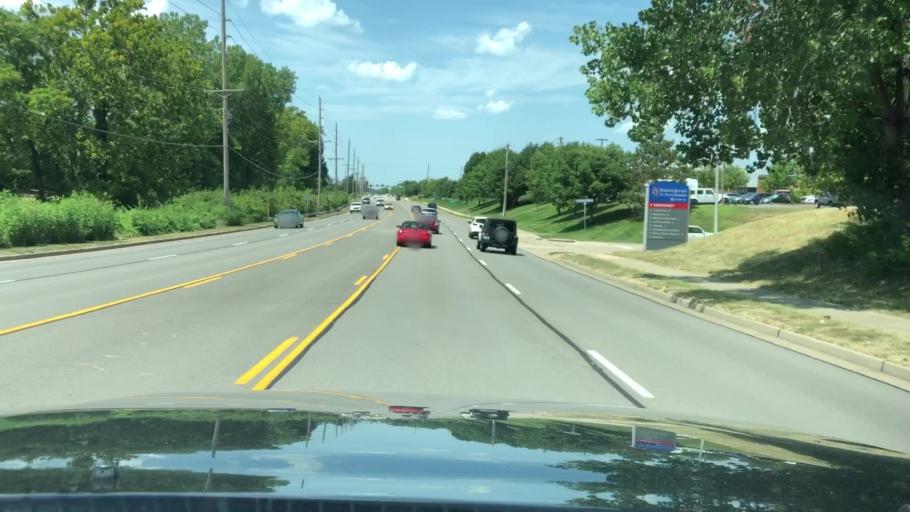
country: US
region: Missouri
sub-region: Saint Charles County
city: Saint Peters
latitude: 38.7918
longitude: -90.5790
